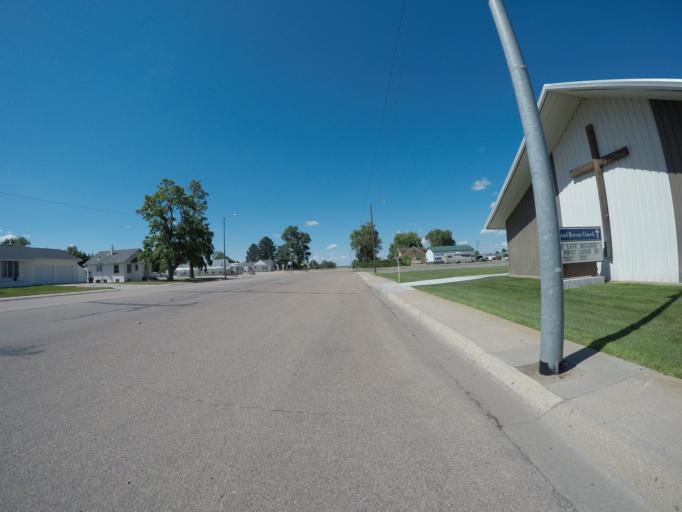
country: US
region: Nebraska
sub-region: Chase County
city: Imperial
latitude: 40.5272
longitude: -101.6431
